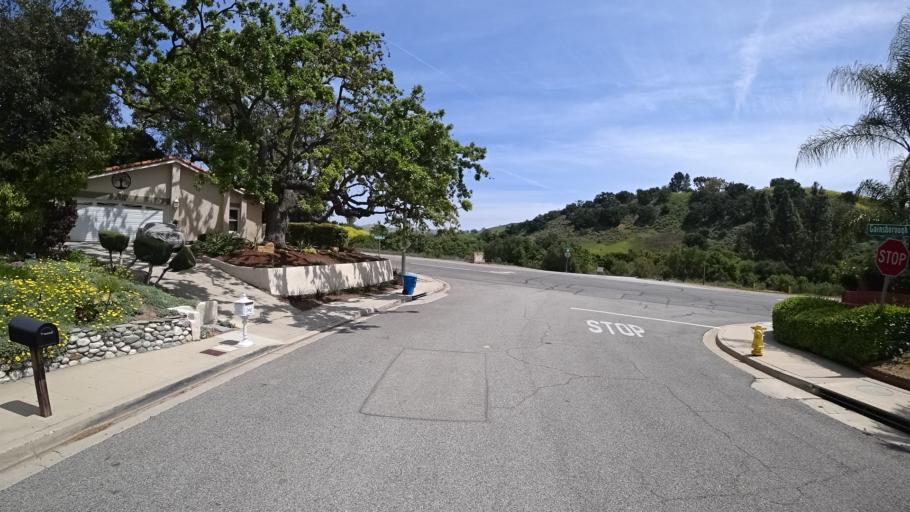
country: US
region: California
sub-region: Ventura County
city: Thousand Oaks
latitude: 34.1941
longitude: -118.8870
